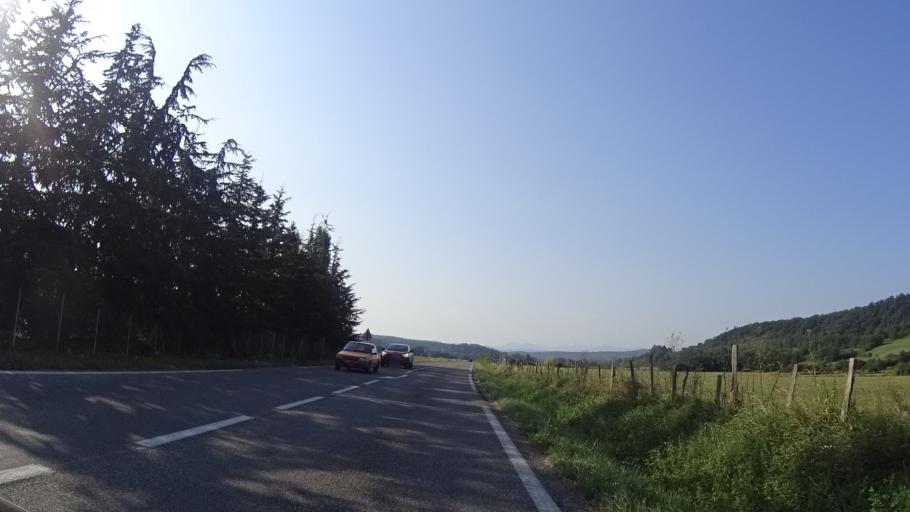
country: FR
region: Midi-Pyrenees
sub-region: Departement de l'Ariege
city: Mirepoix
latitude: 43.0453
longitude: 1.8947
